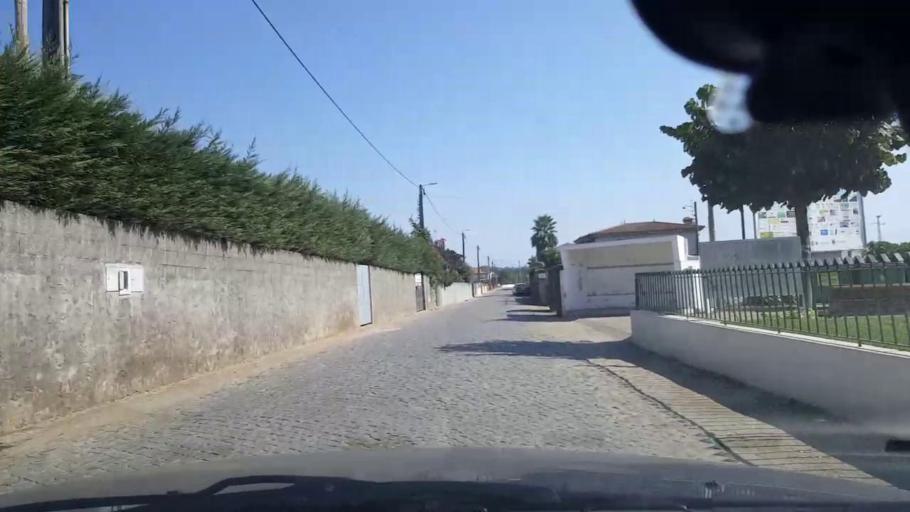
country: PT
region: Porto
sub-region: Povoa de Varzim
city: Pedroso
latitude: 41.4134
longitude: -8.7001
